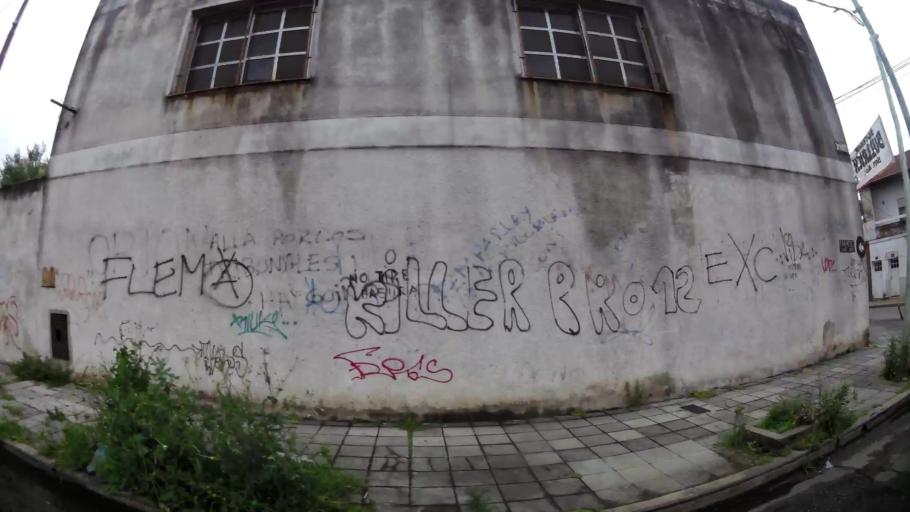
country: AR
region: Buenos Aires
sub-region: Partido de Lanus
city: Lanus
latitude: -34.6996
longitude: -58.3849
